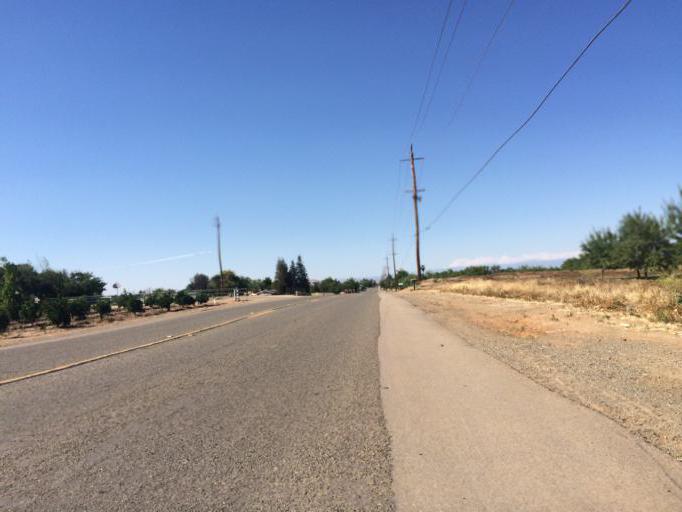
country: US
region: California
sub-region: Fresno County
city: Sanger
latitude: 36.7761
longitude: -119.6101
